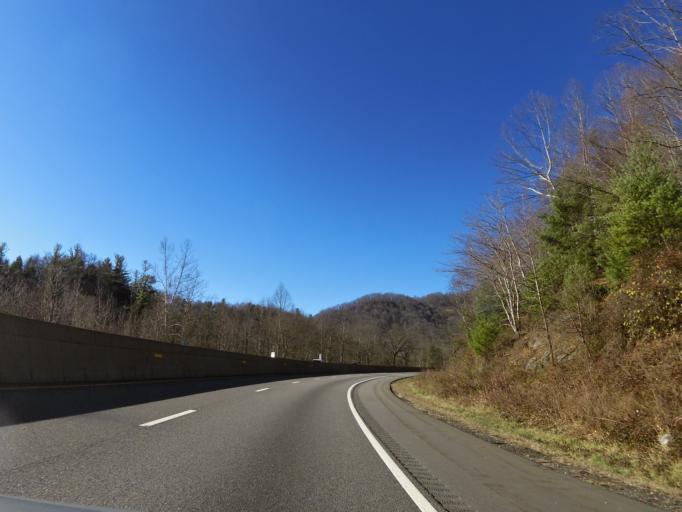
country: US
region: North Carolina
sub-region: Haywood County
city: Cove Creek
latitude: 35.6282
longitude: -82.9998
